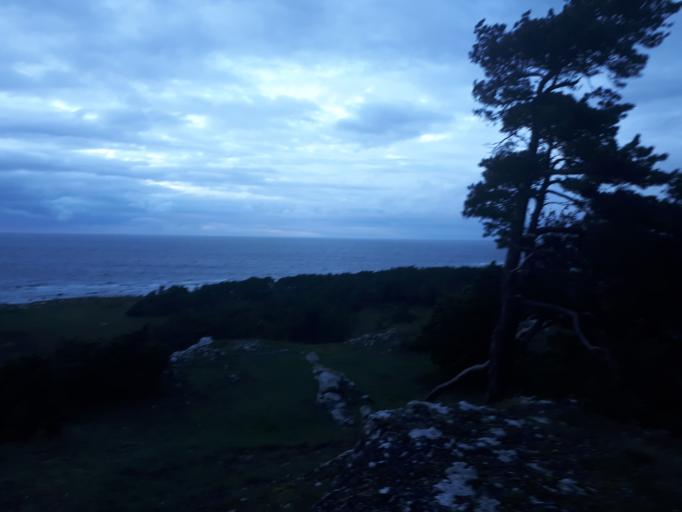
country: SE
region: Gotland
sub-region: Gotland
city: Visby
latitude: 57.6849
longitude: 18.3480
